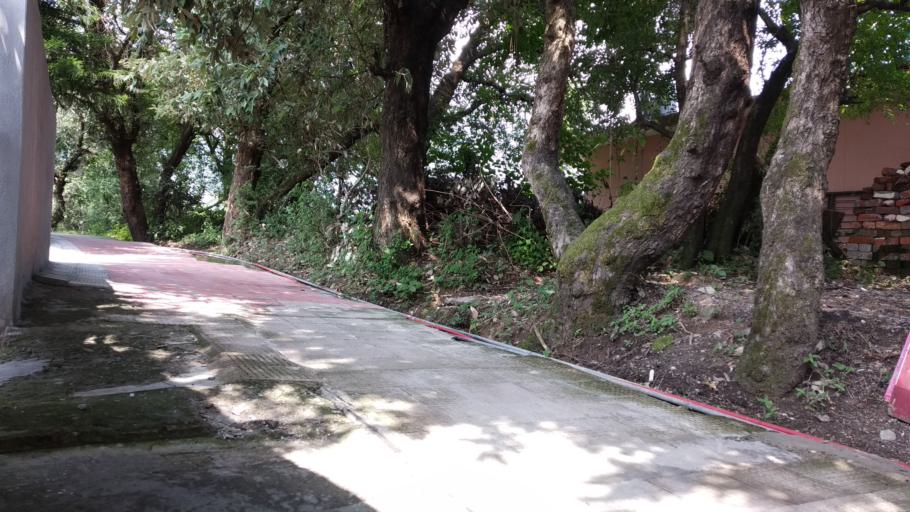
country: IN
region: Himachal Pradesh
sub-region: Kangra
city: Dharmsala
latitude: 32.1725
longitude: 76.3886
